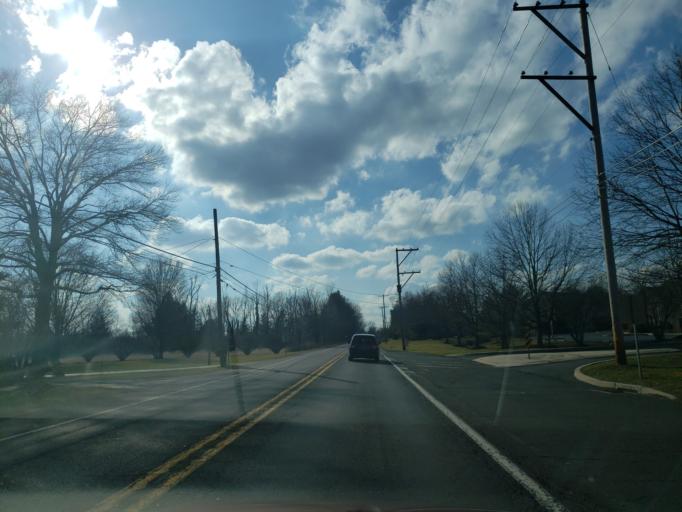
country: US
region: Pennsylvania
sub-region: Bucks County
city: Doylestown
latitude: 40.3183
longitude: -75.0946
